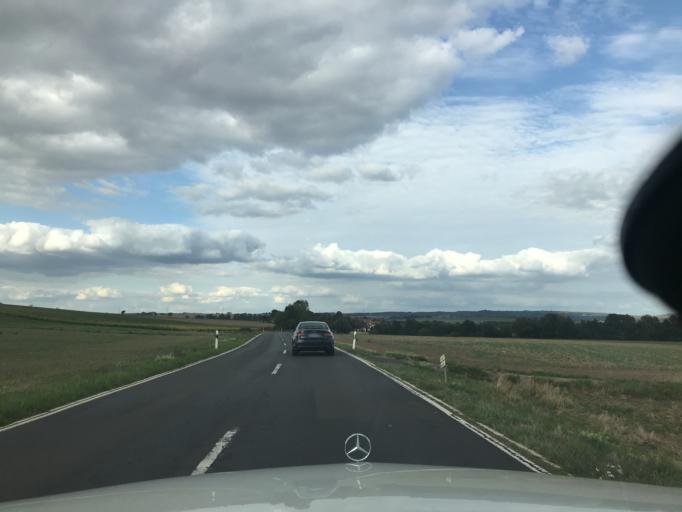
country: DE
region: Hesse
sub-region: Regierungsbezirk Kassel
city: Calden
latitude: 51.4196
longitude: 9.4184
